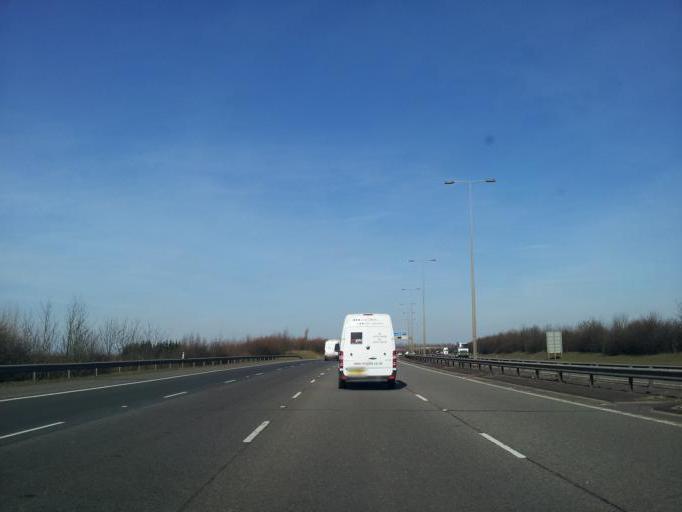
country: GB
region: England
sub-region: Cambridgeshire
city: Stilton
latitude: 52.4803
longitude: -0.2870
